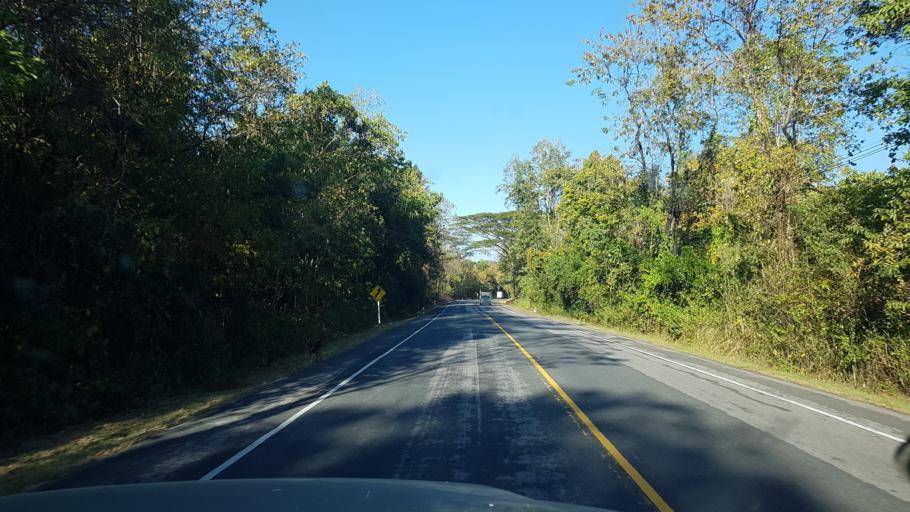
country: TH
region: Phetchabun
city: Lom Sak
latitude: 16.7492
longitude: 101.4527
